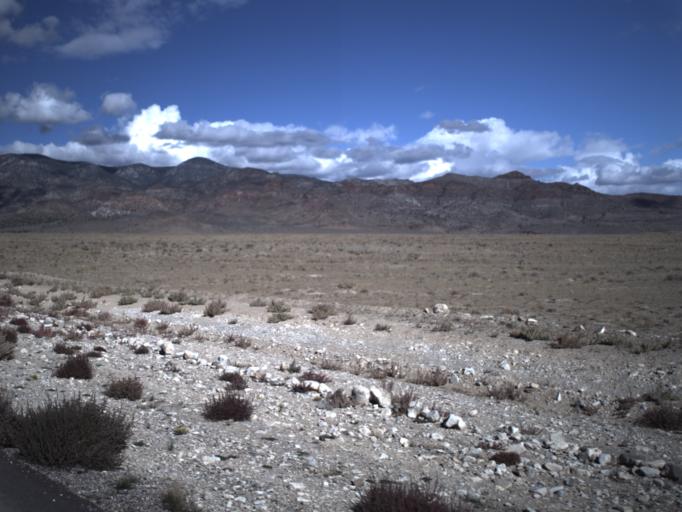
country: US
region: Utah
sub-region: Beaver County
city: Milford
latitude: 38.4876
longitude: -113.4596
